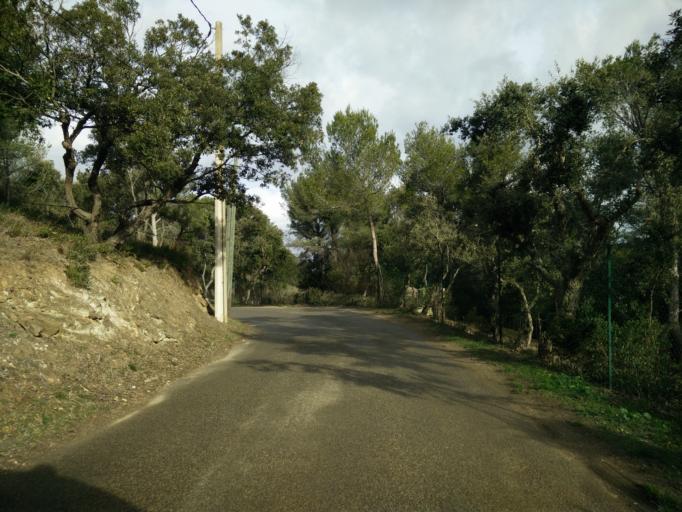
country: FR
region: Provence-Alpes-Cote d'Azur
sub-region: Departement du Var
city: Six-Fours-les-Plages
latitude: 43.0643
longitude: 5.8282
